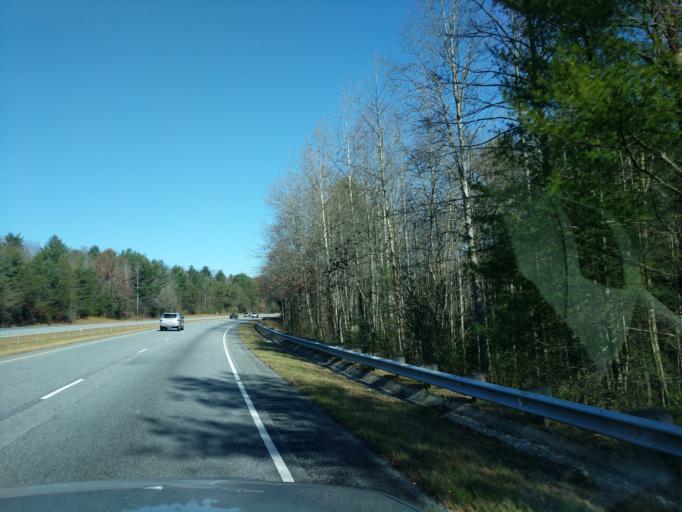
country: US
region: North Carolina
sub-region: Henderson County
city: Flat Rock
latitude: 35.2054
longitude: -82.4503
